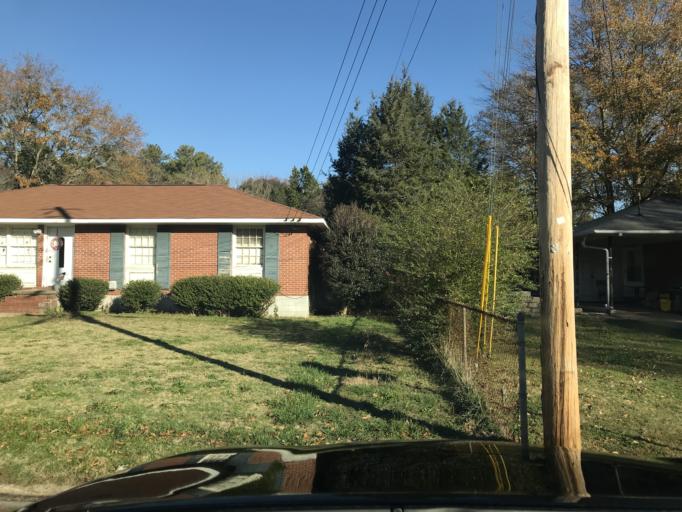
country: US
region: Georgia
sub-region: Clayton County
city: Morrow
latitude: 33.5578
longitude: -84.3679
